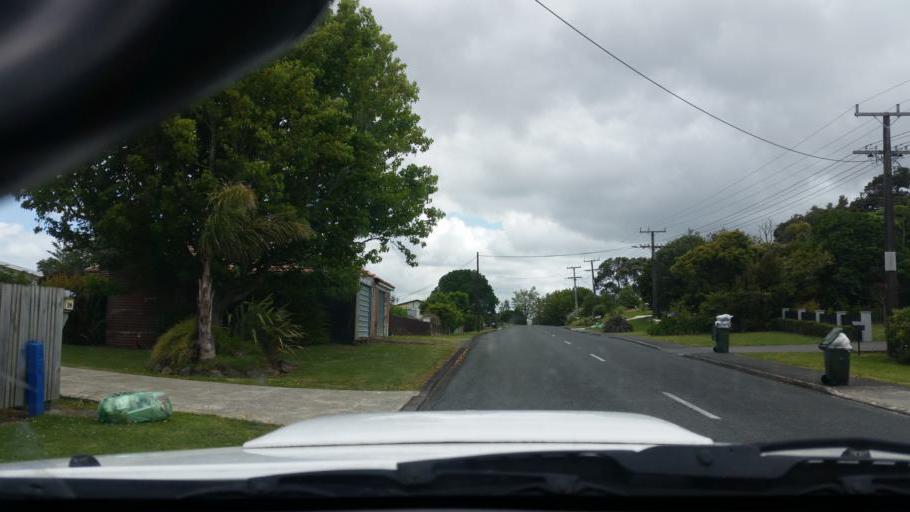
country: NZ
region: Northland
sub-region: Whangarei
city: Ruakaka
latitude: -36.1153
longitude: 174.3497
